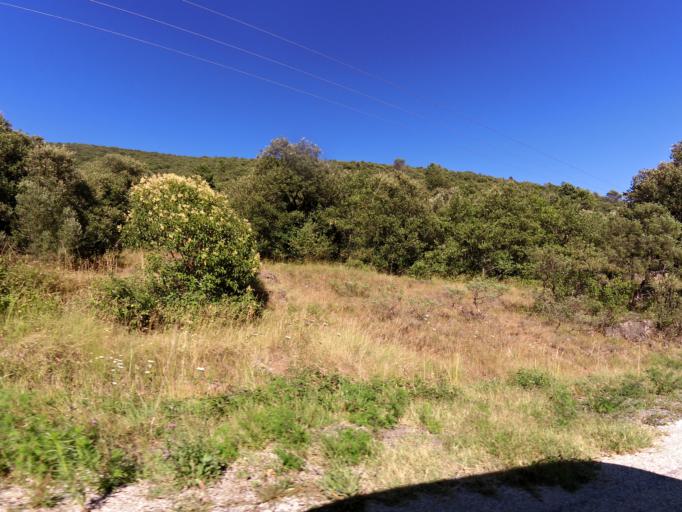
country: FR
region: Languedoc-Roussillon
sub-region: Departement du Gard
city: Saint-Jean-du-Gard
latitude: 44.0877
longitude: 3.9181
